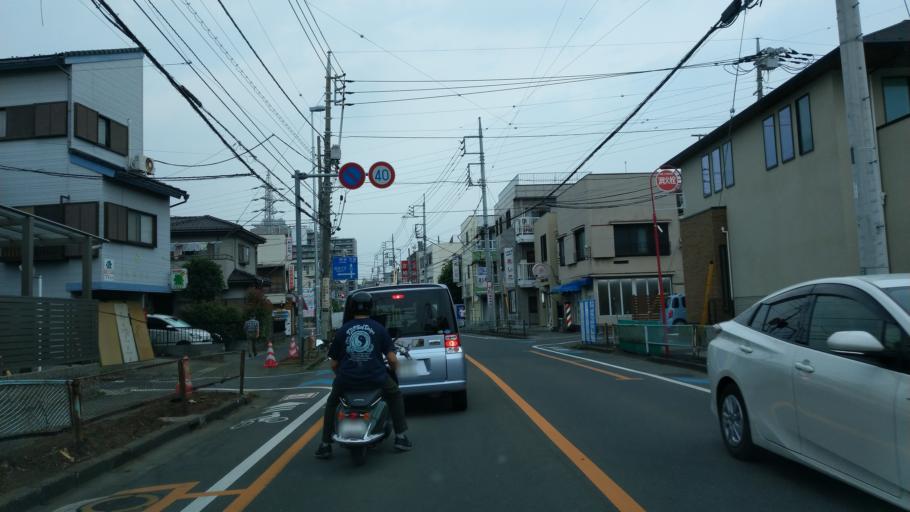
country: JP
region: Saitama
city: Yono
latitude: 35.8814
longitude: 139.6426
